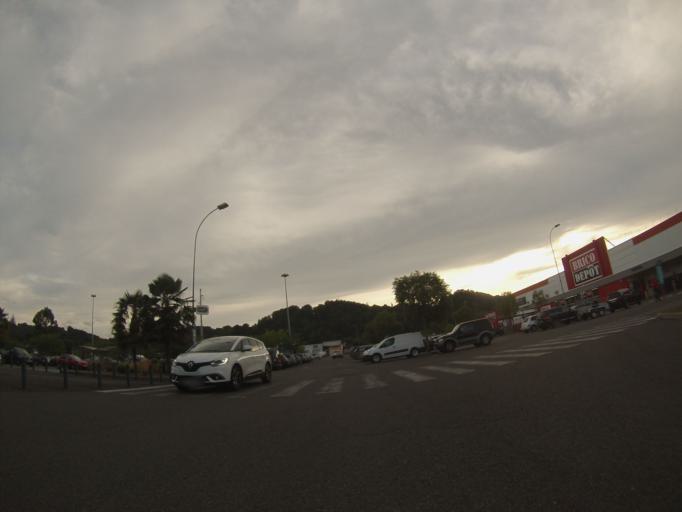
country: FR
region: Aquitaine
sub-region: Departement des Pyrenees-Atlantiques
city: Gelos
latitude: 43.2809
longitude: -0.3610
